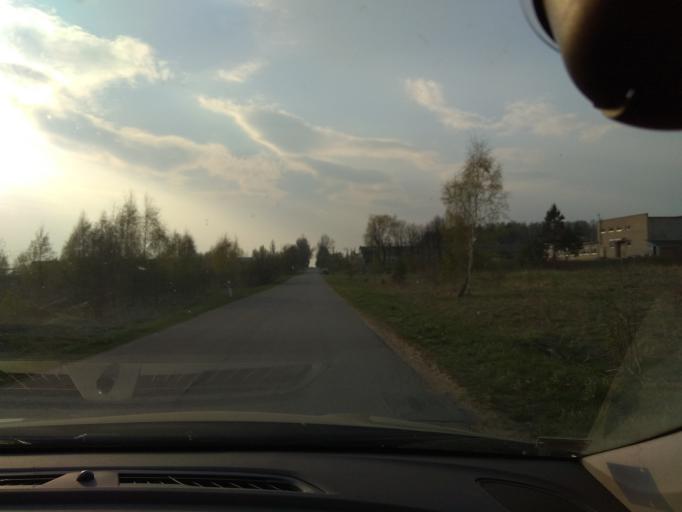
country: LT
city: Baltoji Voke
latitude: 54.5960
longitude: 25.1489
